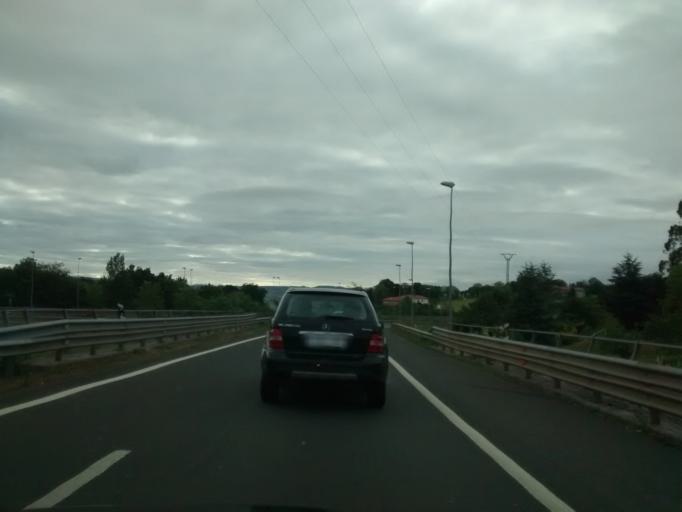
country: ES
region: Cantabria
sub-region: Provincia de Cantabria
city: Torrelavega
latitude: 43.3500
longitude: -4.0334
